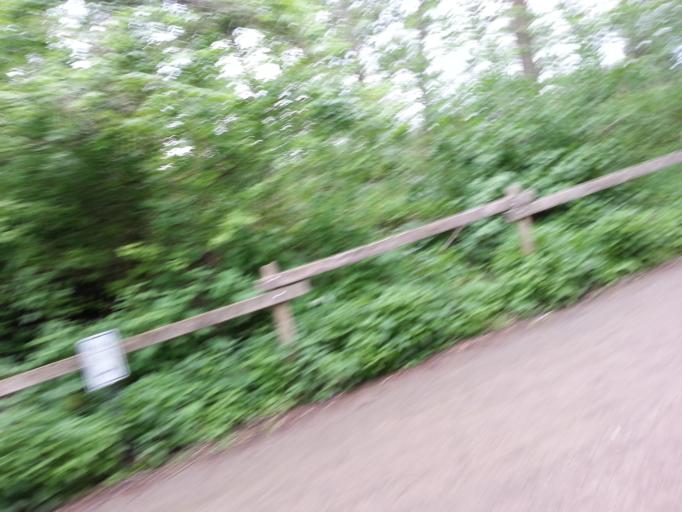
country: DE
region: Berlin
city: Charlottenburg-Nord
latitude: 52.5286
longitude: 13.2932
